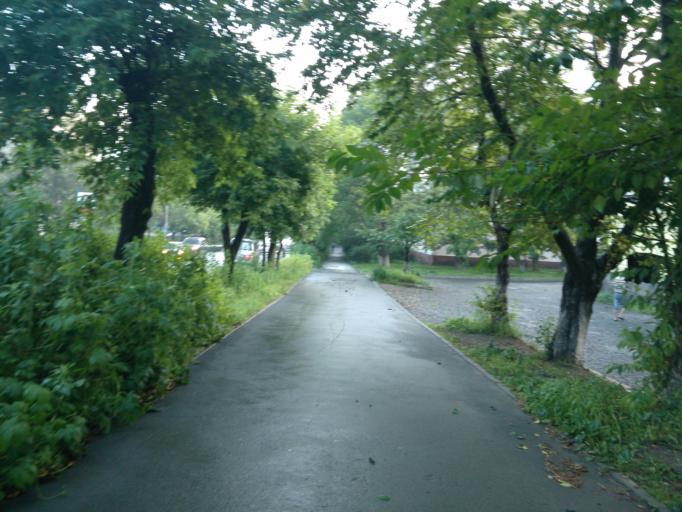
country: RU
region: Primorskiy
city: Vladivostok
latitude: 43.0920
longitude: 131.9667
